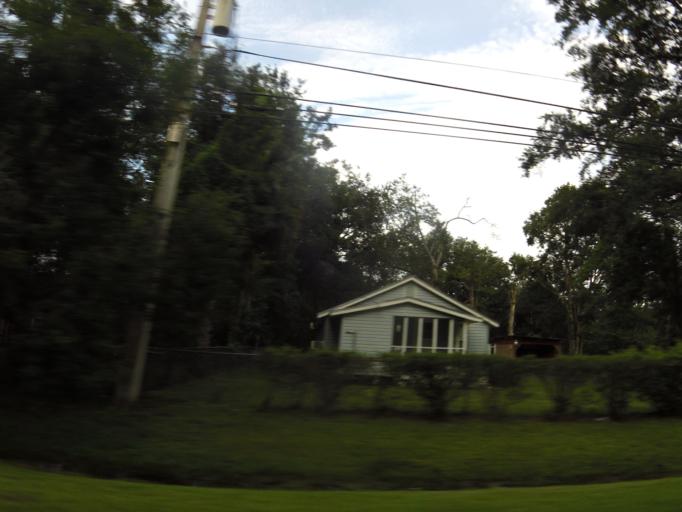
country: US
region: Florida
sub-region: Duval County
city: Jacksonville
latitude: 30.3403
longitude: -81.8067
